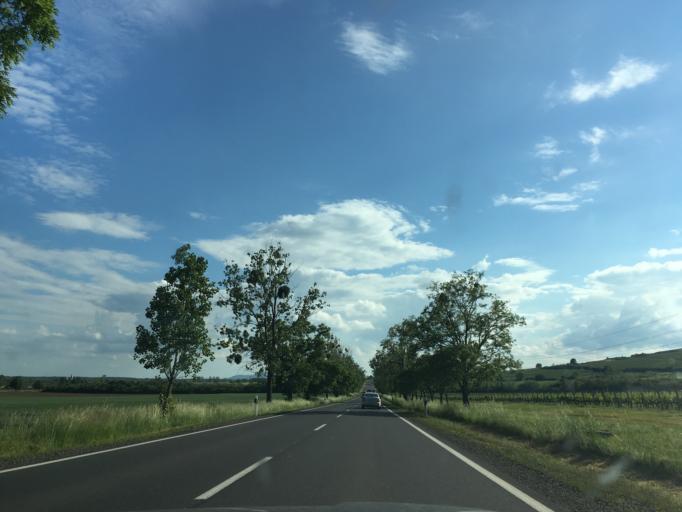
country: HU
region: Borsod-Abauj-Zemplen
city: Tolcsva
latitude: 48.2816
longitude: 21.4983
